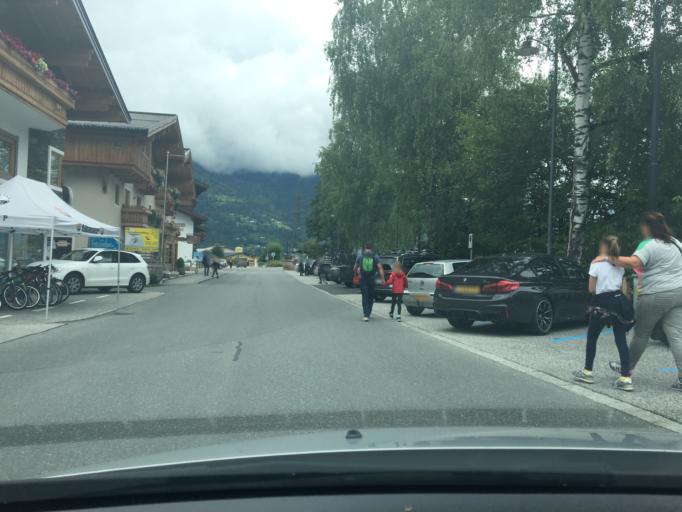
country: AT
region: Salzburg
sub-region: Politischer Bezirk Zell am See
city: Kaprun
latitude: 47.2732
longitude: 12.7589
